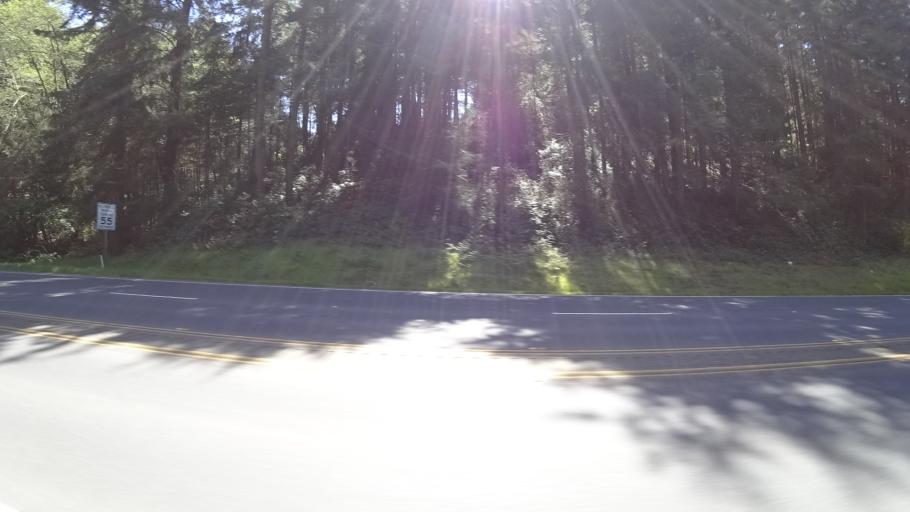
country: US
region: California
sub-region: Humboldt County
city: Westhaven-Moonstone
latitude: 41.1393
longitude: -124.1390
